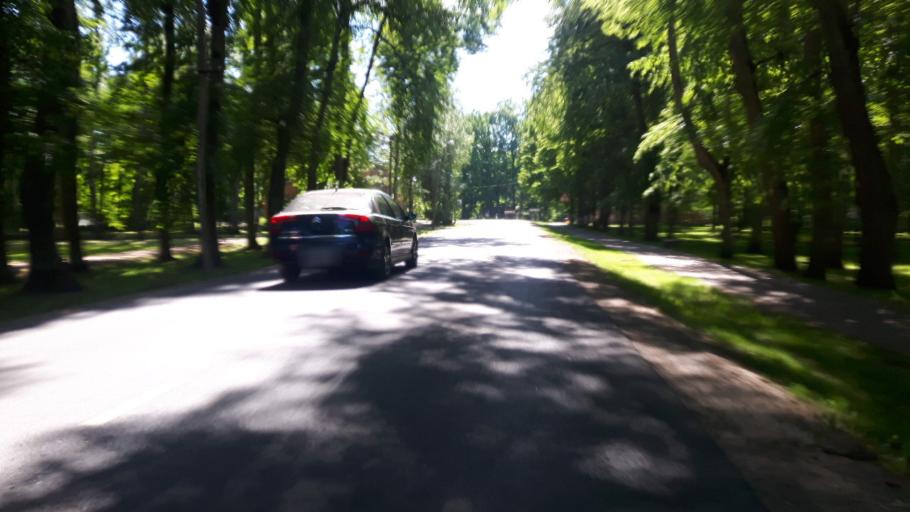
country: EE
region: Paernumaa
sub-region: Sindi linn
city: Sindi
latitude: 58.4052
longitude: 24.6497
